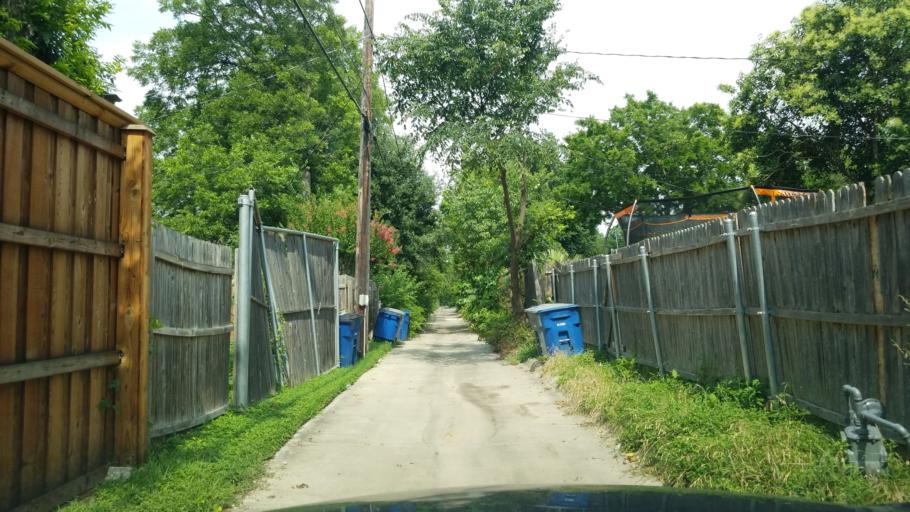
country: US
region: Texas
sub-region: Dallas County
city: Farmers Branch
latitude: 32.9009
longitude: -96.8805
